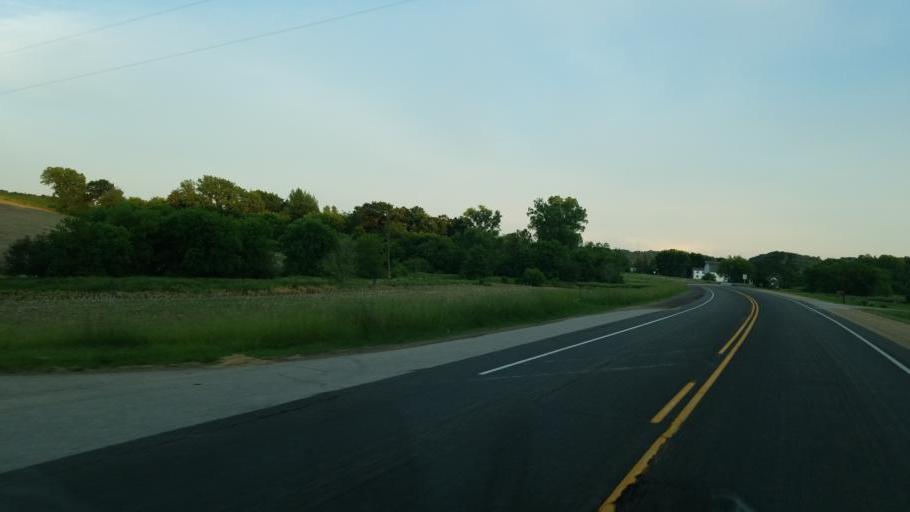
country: US
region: Wisconsin
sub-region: Monroe County
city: Tomah
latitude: 43.9305
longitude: -90.5033
